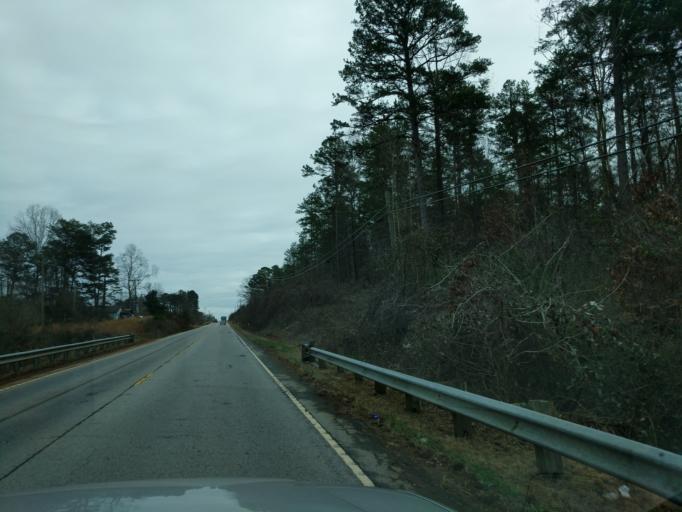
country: US
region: South Carolina
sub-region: Oconee County
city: Westminster
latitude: 34.6858
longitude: -83.1358
